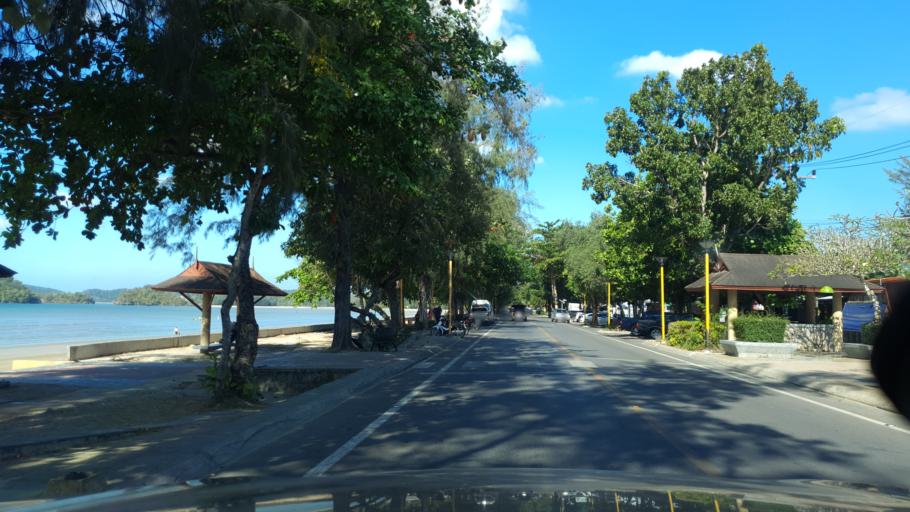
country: TH
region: Phangnga
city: Ban Ao Nang
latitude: 8.0427
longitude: 98.8104
